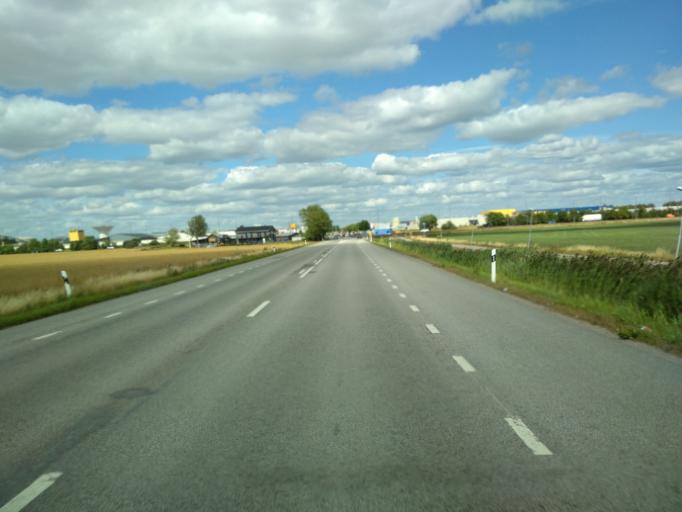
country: SE
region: Uppsala
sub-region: Uppsala Kommun
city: Saevja
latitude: 59.8404
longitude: 17.6895
